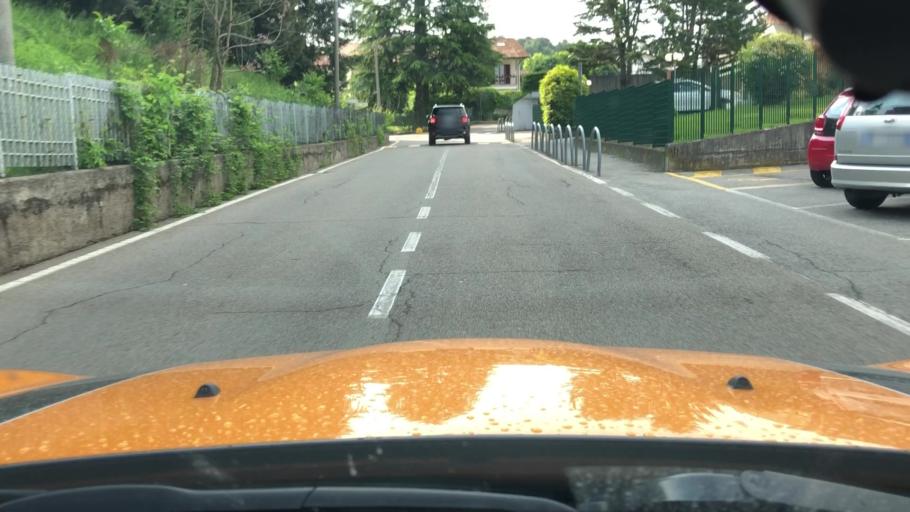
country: IT
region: Lombardy
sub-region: Provincia di Como
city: Senna Comasco
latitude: 45.7629
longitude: 9.1111
